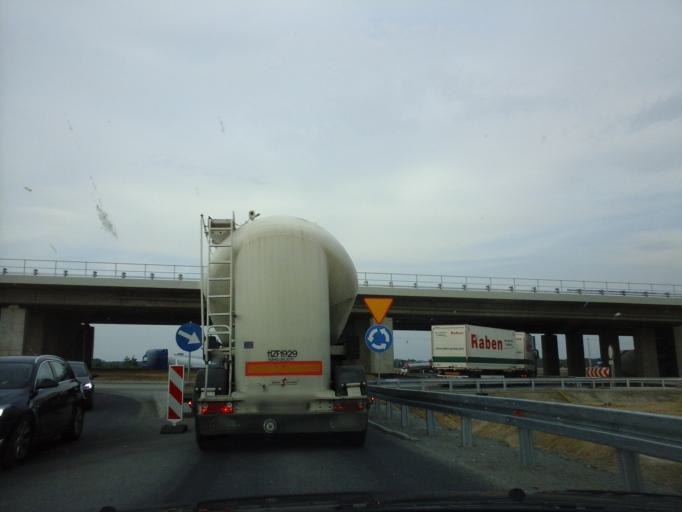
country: PL
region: Lower Silesian Voivodeship
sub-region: Powiat trzebnicki
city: Zmigrod
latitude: 51.4923
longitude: 16.9040
